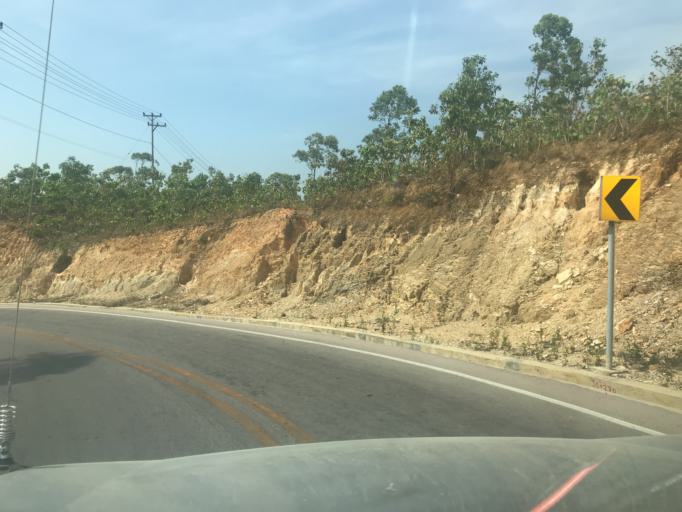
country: TL
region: Aileu
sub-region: Aileu Villa
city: Aileu
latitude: -8.6615
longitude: 125.5596
